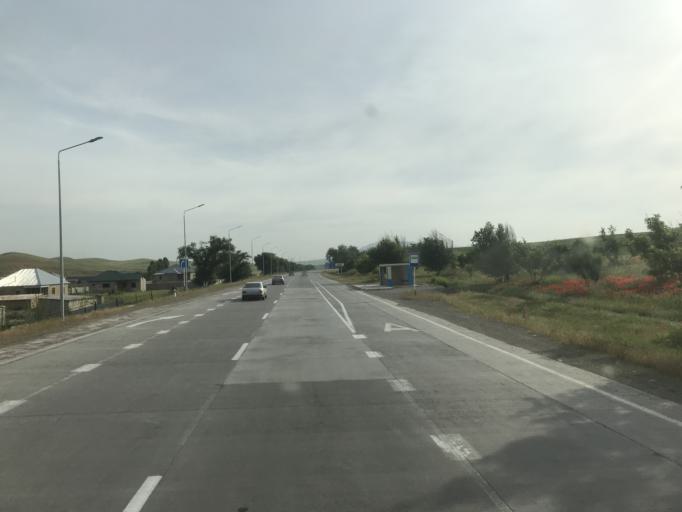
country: KZ
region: Ongtustik Qazaqstan
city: Qazyqurt
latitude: 41.9072
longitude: 69.4662
